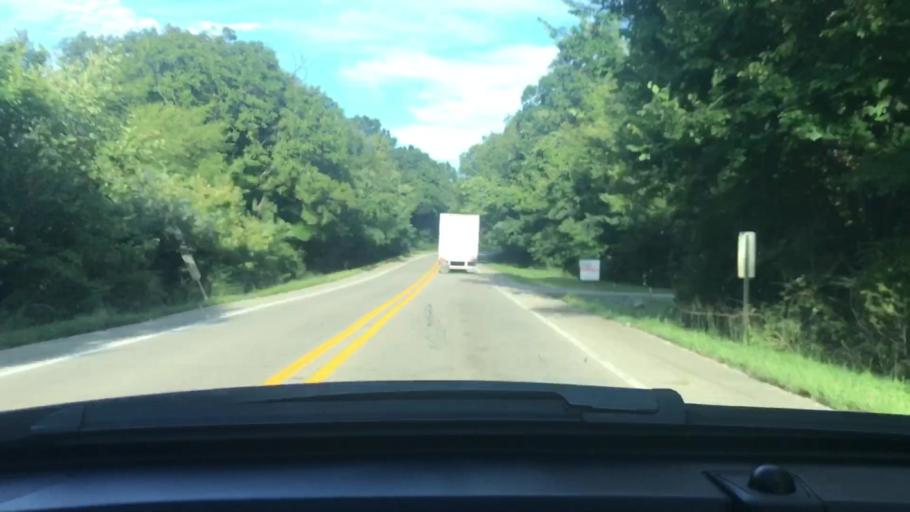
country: US
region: Arkansas
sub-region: Randolph County
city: Pocahontas
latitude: 36.2127
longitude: -91.2086
